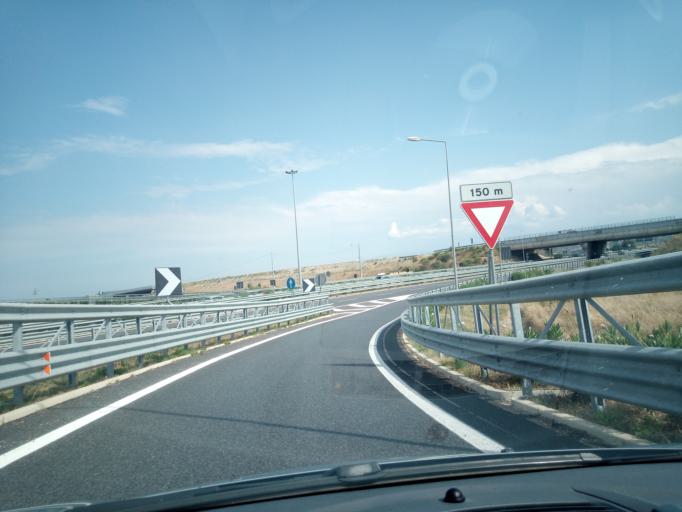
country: IT
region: Calabria
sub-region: Provincia di Cosenza
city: Firmo
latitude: 39.7228
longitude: 16.2380
